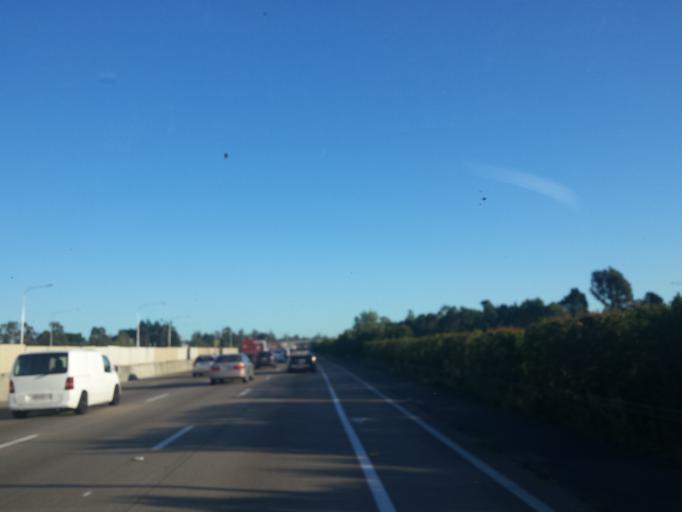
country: AU
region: Queensland
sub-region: Gold Coast
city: Oxenford
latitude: -27.8638
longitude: 153.3115
